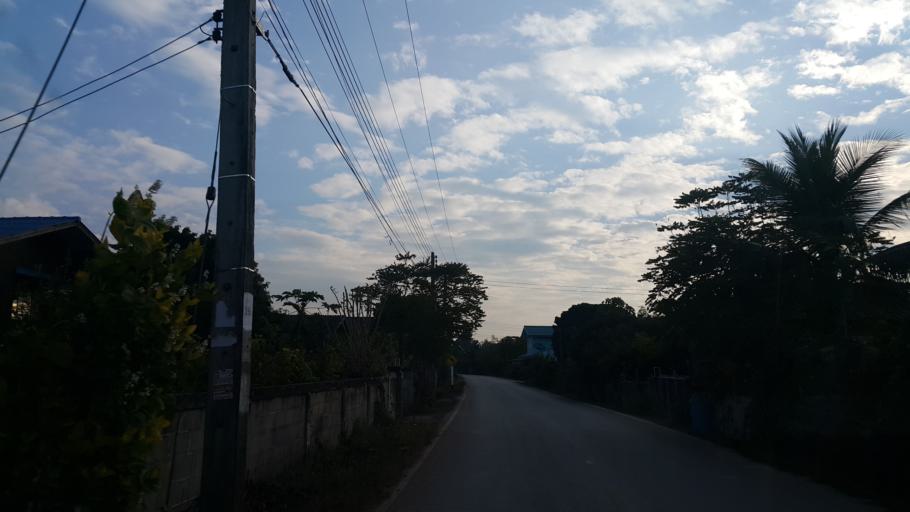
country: TH
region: Lampang
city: Sop Prap
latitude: 17.9038
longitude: 99.3292
